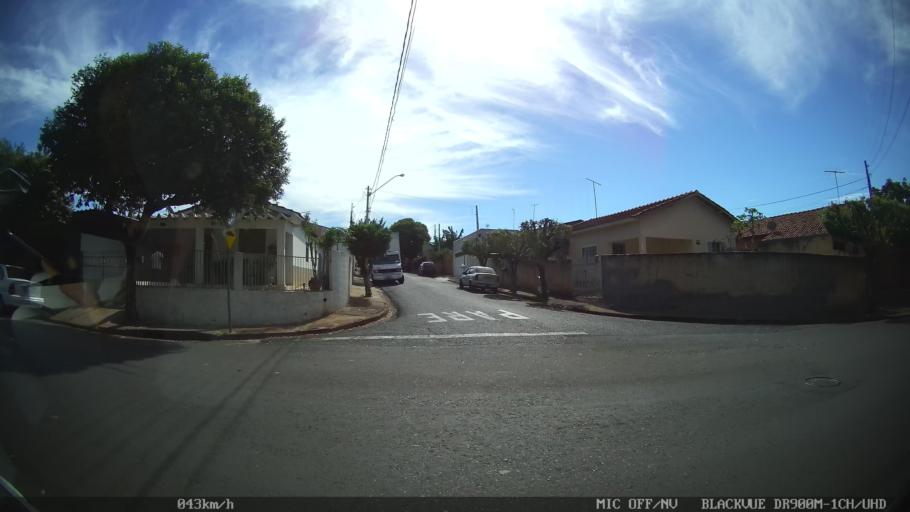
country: BR
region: Sao Paulo
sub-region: Sao Jose Do Rio Preto
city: Sao Jose do Rio Preto
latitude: -20.8390
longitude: -49.3478
